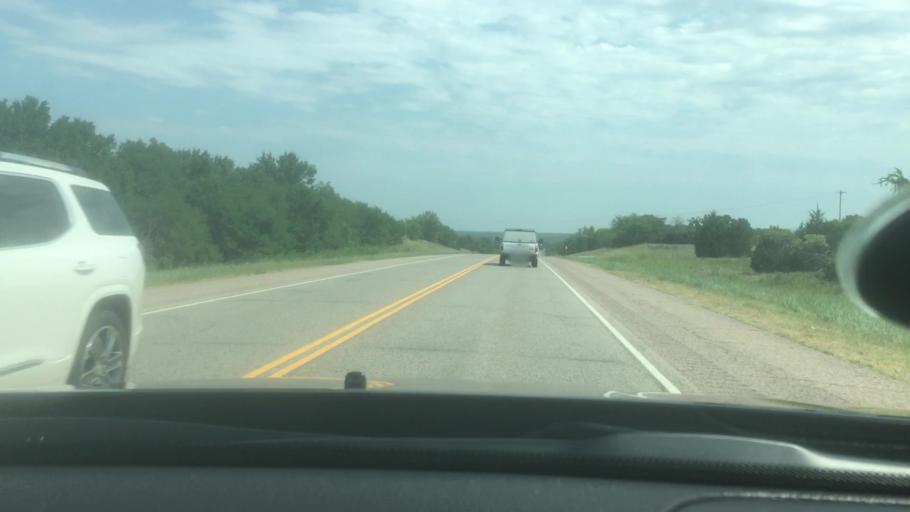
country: US
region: Oklahoma
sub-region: Seminole County
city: Maud
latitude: 35.0567
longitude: -96.9318
